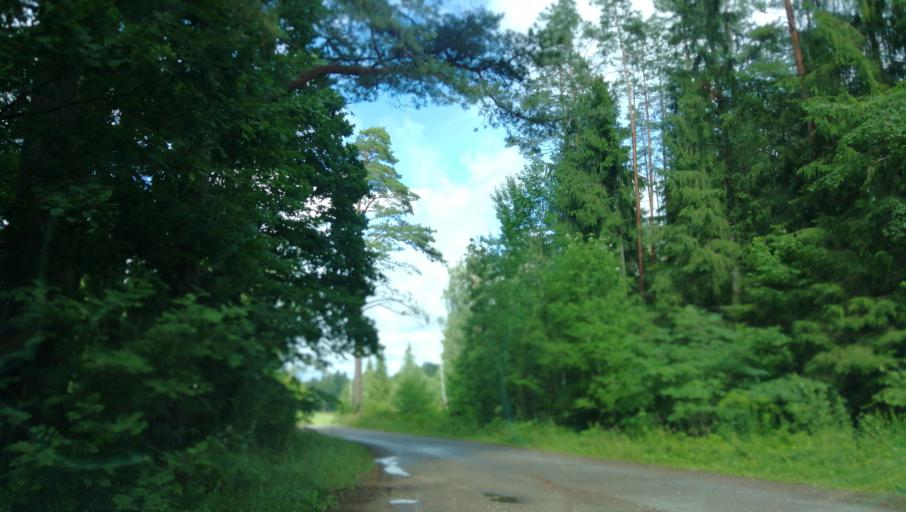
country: LV
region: Cesu Rajons
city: Cesis
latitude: 57.3104
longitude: 25.2187
